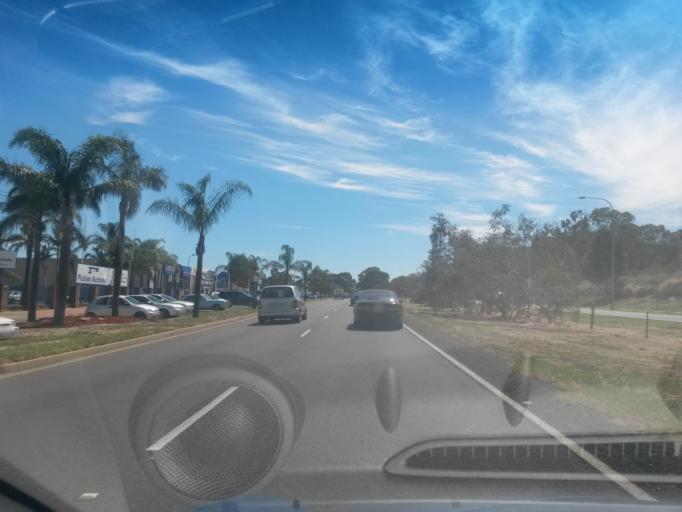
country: AU
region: South Australia
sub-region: Salisbury
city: Salisbury
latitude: -34.7705
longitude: 138.6656
